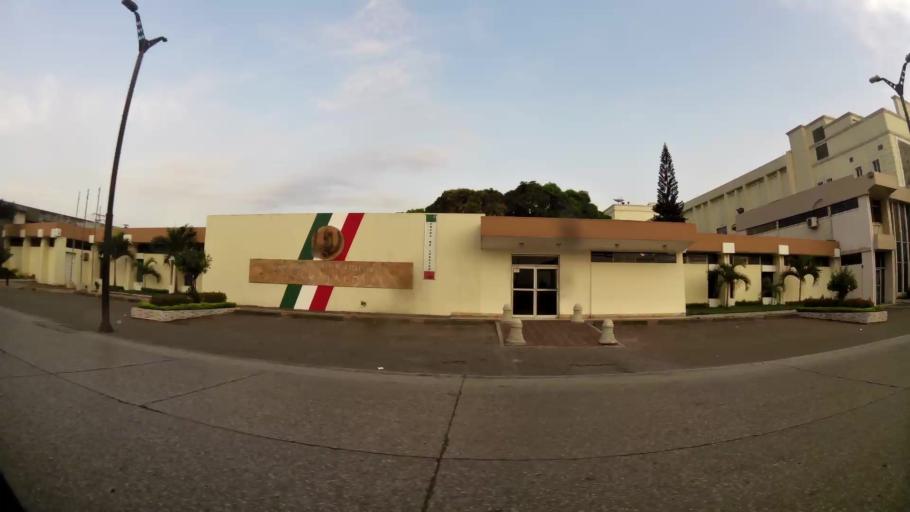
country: EC
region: Guayas
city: Eloy Alfaro
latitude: -2.1688
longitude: -79.8920
